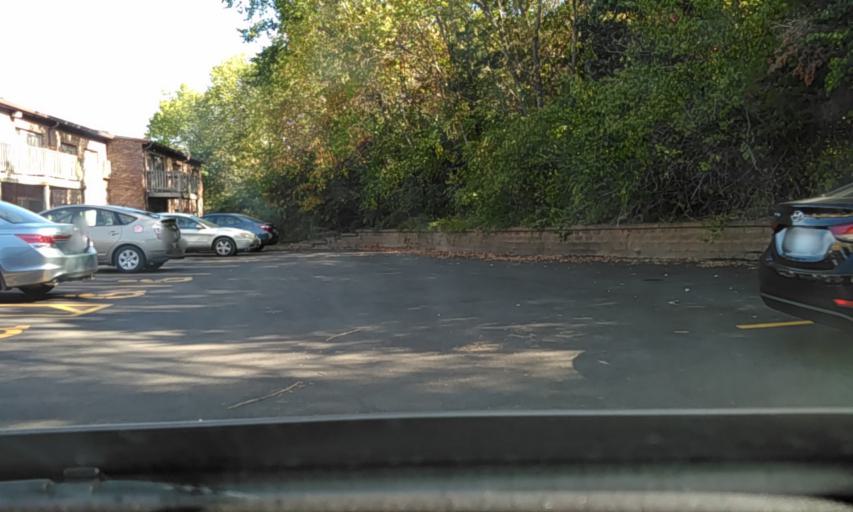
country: US
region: Missouri
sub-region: Saint Louis County
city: Mehlville
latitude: 38.4869
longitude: -90.3504
